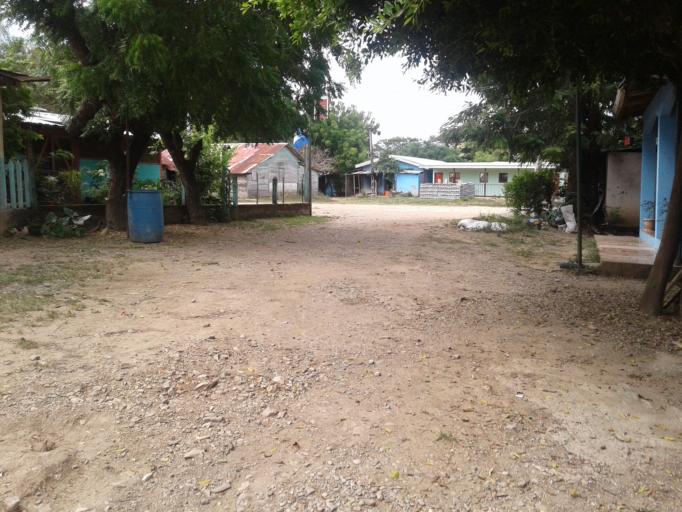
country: CR
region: Guanacaste
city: La Cruz
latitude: 11.1114
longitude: -85.7606
